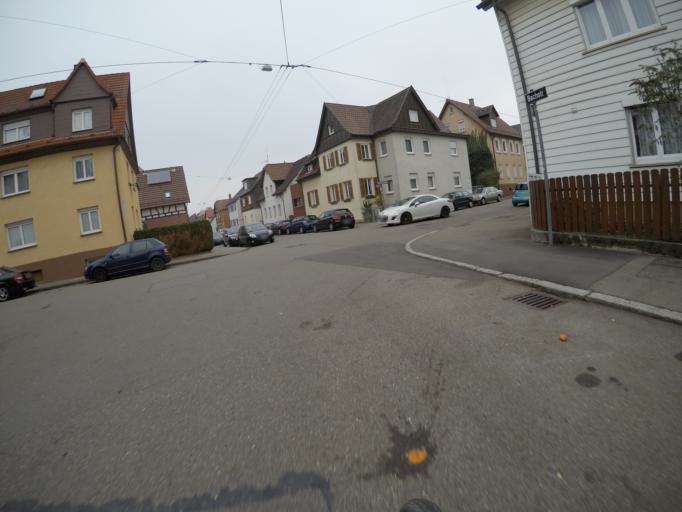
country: DE
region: Baden-Wuerttemberg
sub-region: Regierungsbezirk Stuttgart
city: Steinenbronn
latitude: 48.7314
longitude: 9.1043
